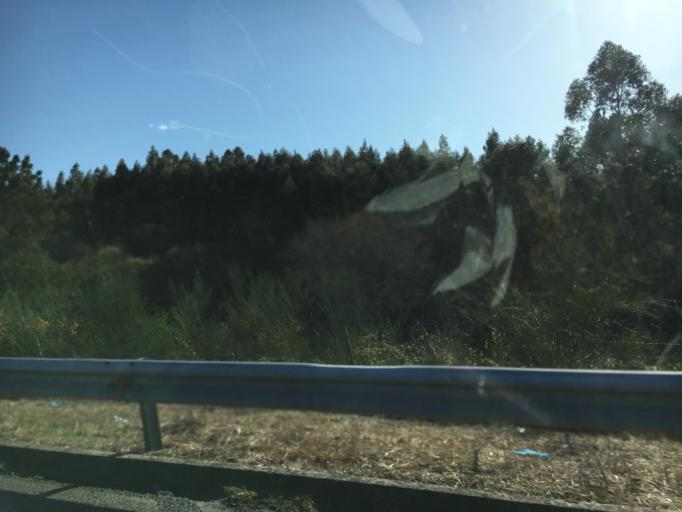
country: ES
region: Galicia
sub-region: Provincia da Coruna
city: Aranga
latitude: 43.2225
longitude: -8.0553
